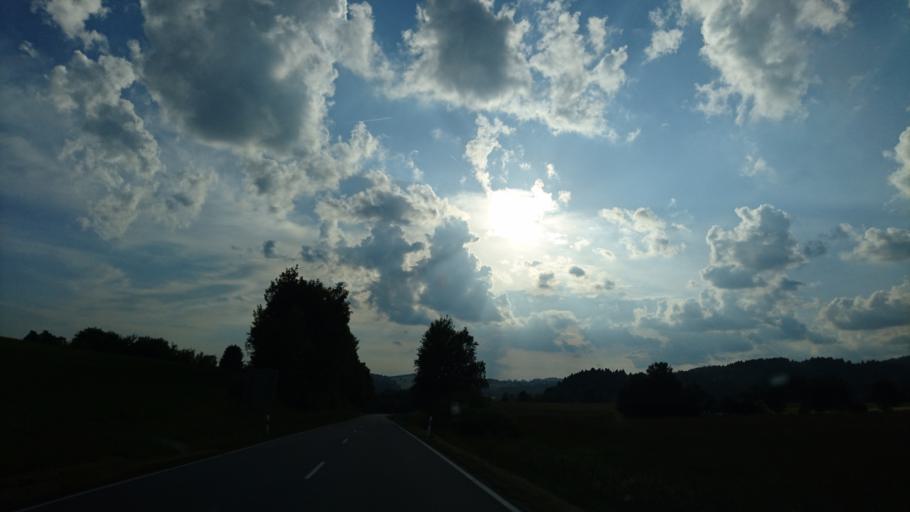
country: DE
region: Bavaria
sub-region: Lower Bavaria
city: Grafenau
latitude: 48.8740
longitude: 13.4194
